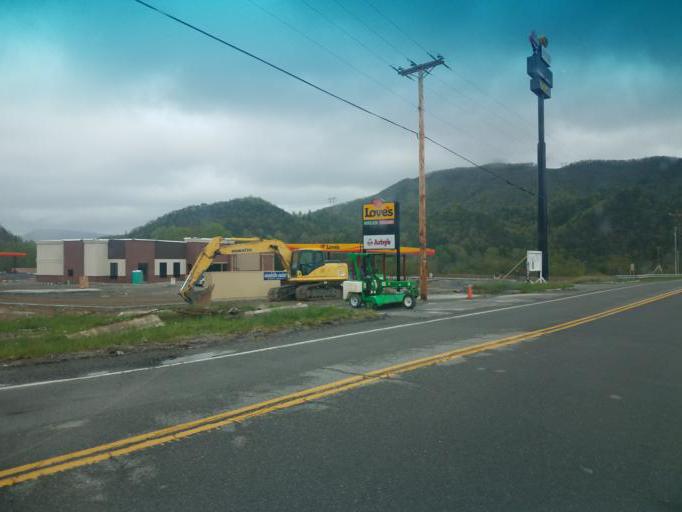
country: US
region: Virginia
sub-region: Bland County
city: Bland
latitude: 37.1777
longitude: -81.1411
